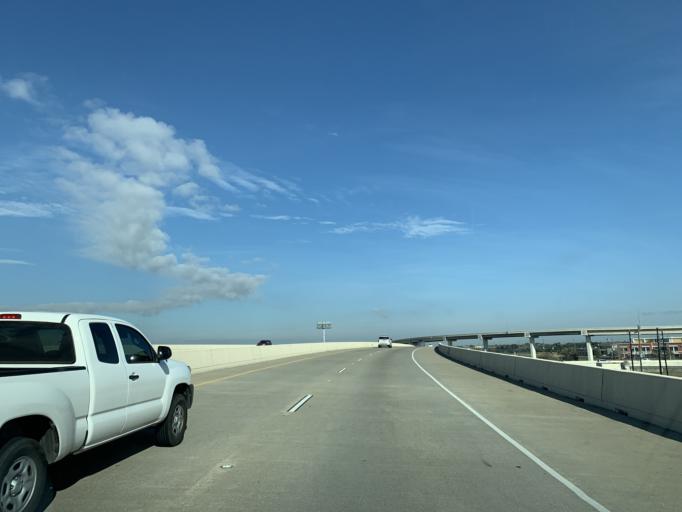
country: US
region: Texas
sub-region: Fort Bend County
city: Cinco Ranch
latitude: 29.6985
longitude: -95.7754
